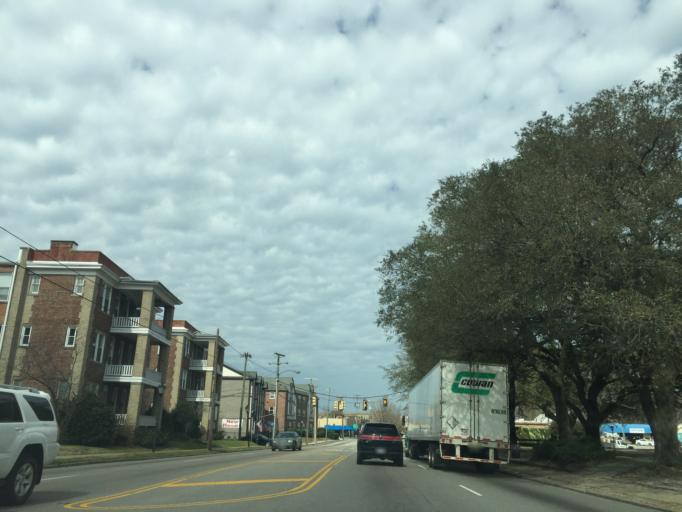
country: US
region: Virginia
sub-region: City of Norfolk
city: Norfolk
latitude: 36.8799
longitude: -76.2821
